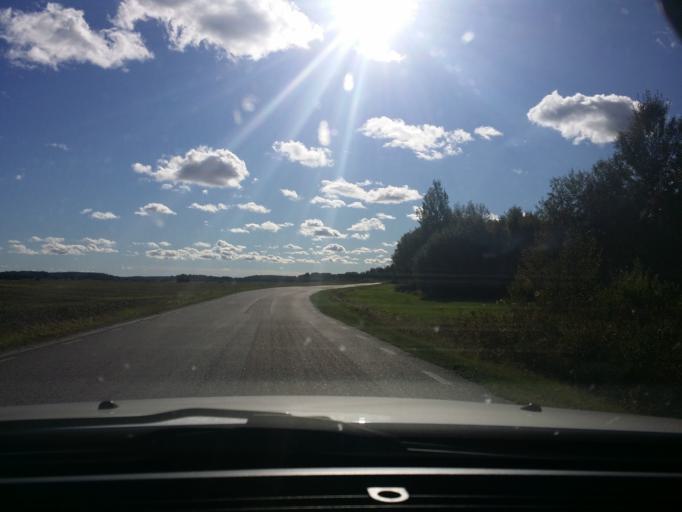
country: SE
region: Vaestmanland
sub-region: Vasteras
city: Vasteras
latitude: 59.5623
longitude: 16.4769
